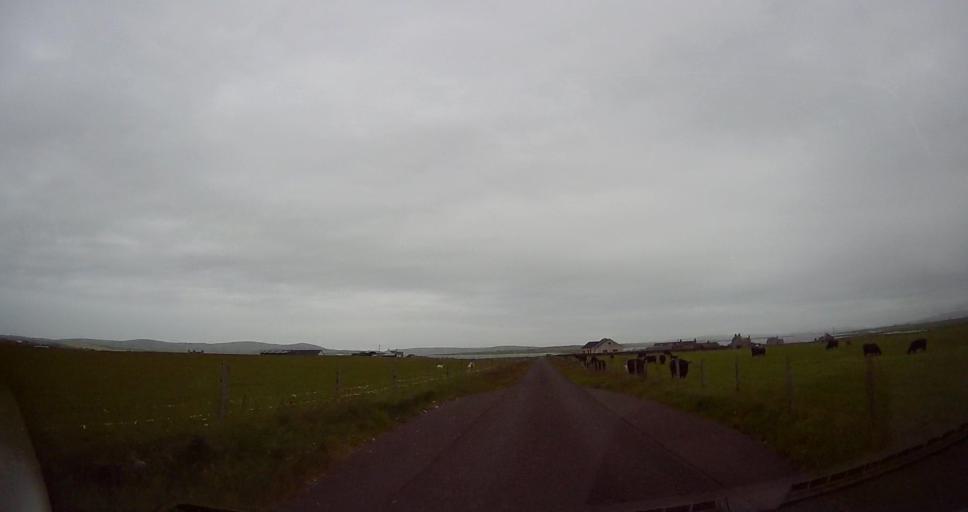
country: GB
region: Scotland
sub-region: Orkney Islands
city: Stromness
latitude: 58.9870
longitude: -3.1934
